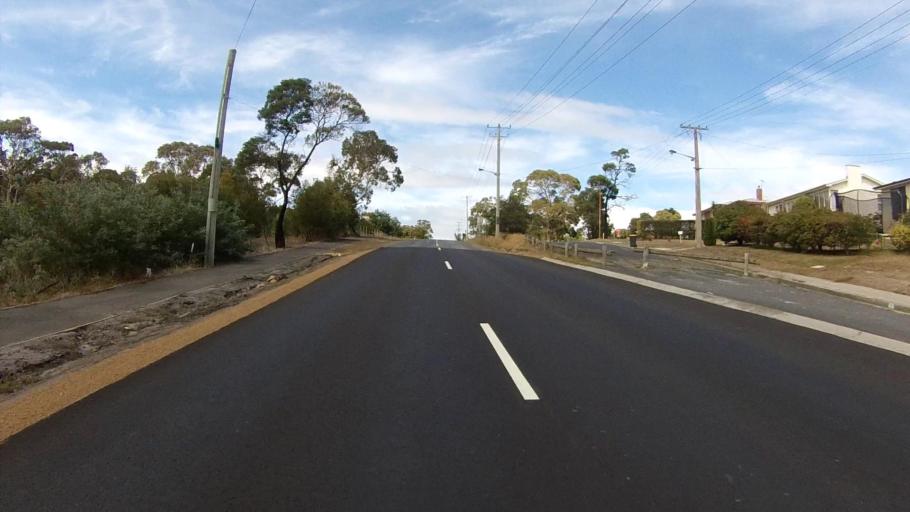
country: AU
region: Tasmania
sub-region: Clarence
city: Lindisfarne
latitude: -42.8151
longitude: 147.3514
